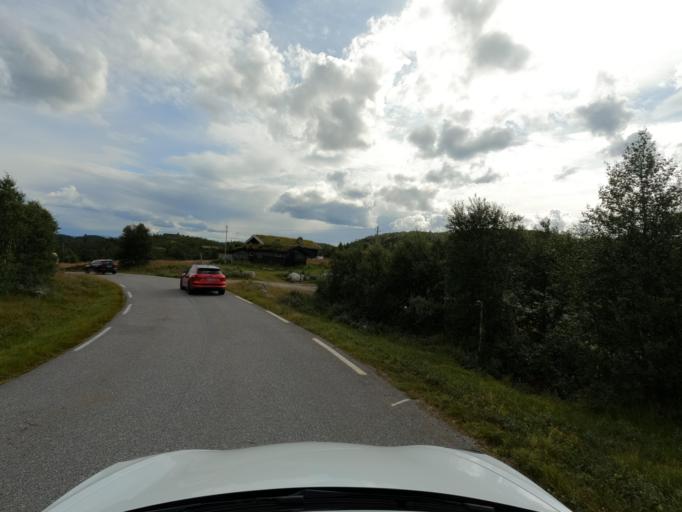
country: NO
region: Telemark
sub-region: Tinn
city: Rjukan
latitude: 59.7995
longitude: 8.7391
